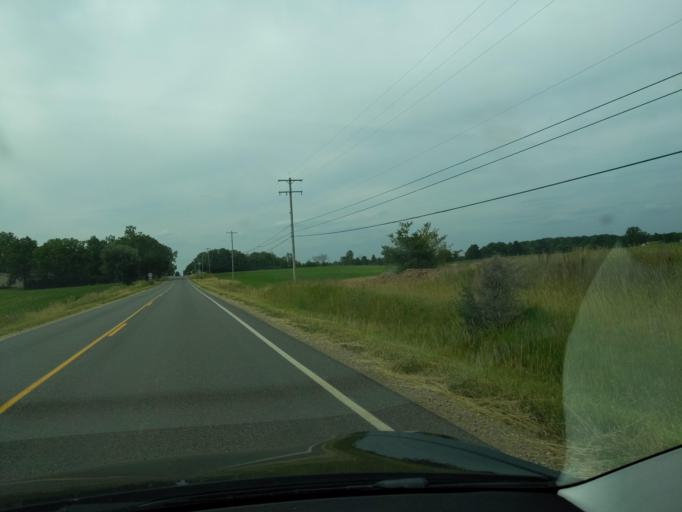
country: US
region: Michigan
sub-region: Clinton County
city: DeWitt
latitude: 42.8433
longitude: -84.6025
